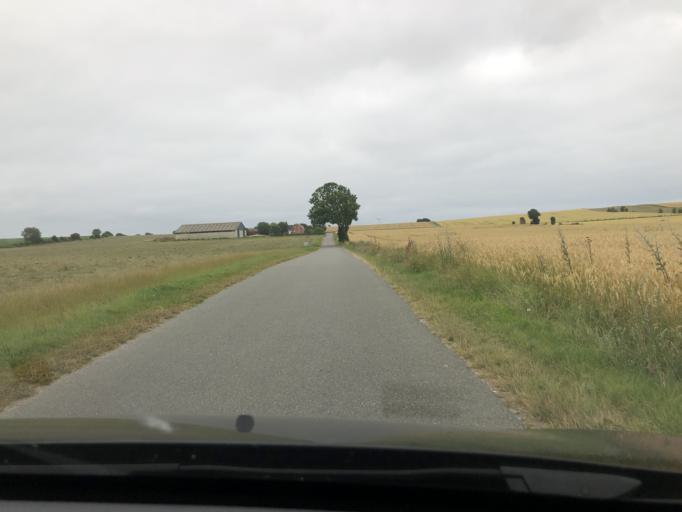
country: DK
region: South Denmark
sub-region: AEro Kommune
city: AEroskobing
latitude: 54.8369
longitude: 10.4176
